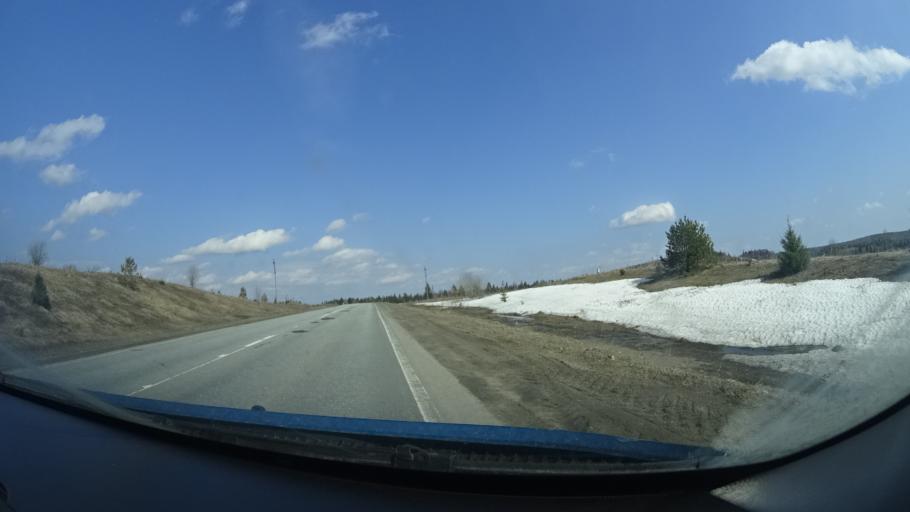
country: RU
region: Perm
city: Yugo-Kamskiy
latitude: 57.7809
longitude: 55.7643
